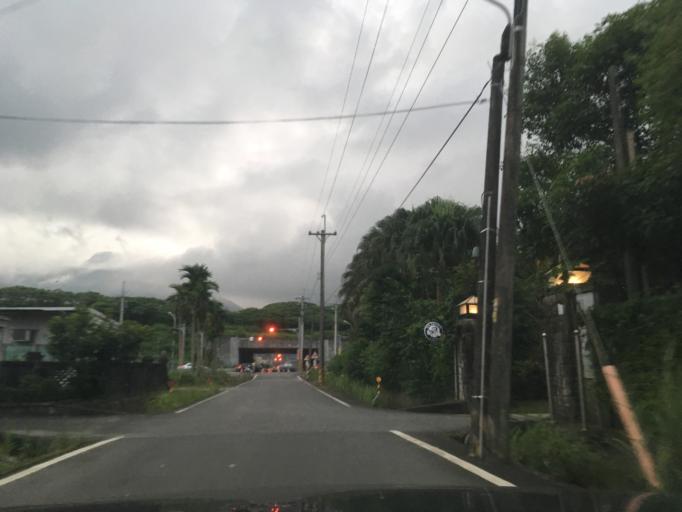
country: TW
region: Taiwan
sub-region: Yilan
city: Yilan
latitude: 24.8217
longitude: 121.7863
